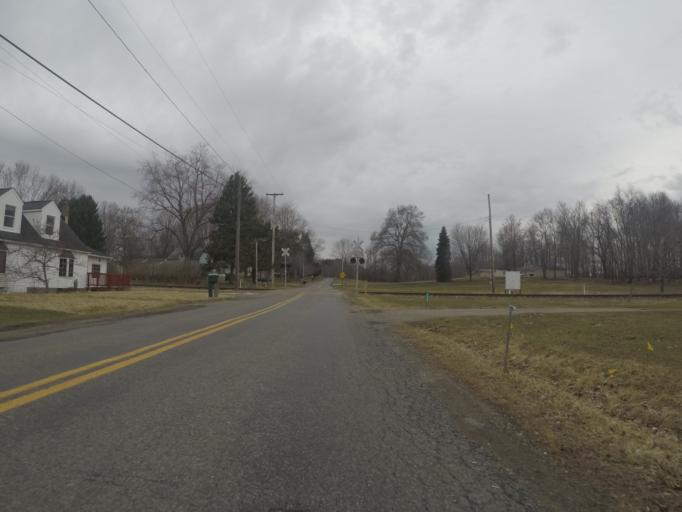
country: US
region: Ohio
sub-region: Portage County
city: Ravenna
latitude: 41.1672
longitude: -81.2831
